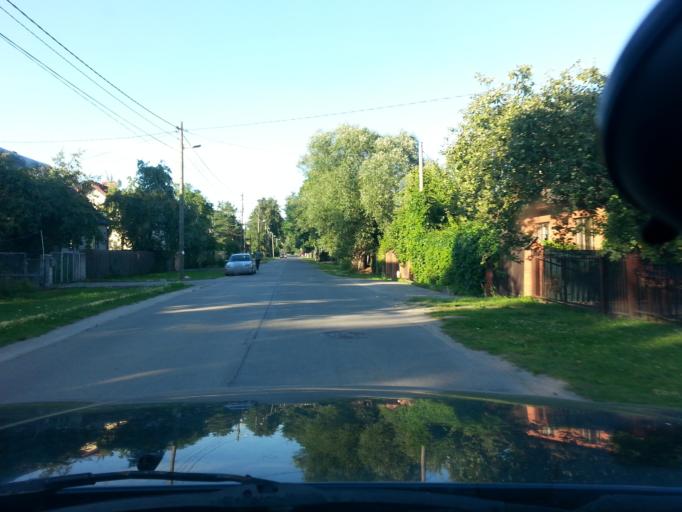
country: LV
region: Riga
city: Riga
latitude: 56.9406
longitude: 24.1896
